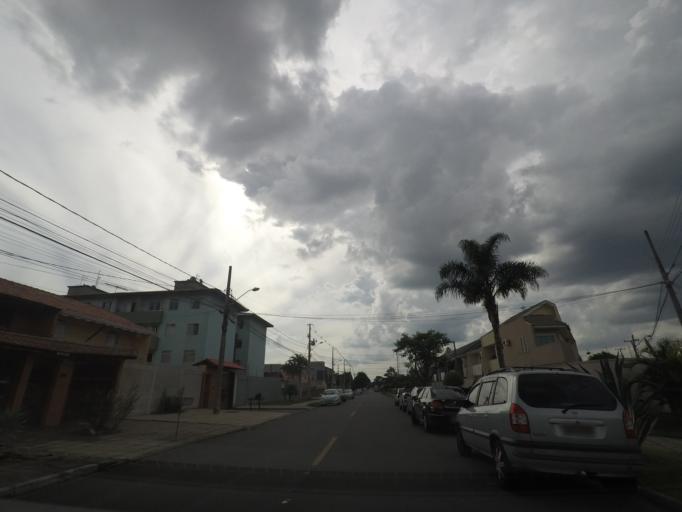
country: BR
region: Parana
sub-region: Sao Jose Dos Pinhais
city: Sao Jose dos Pinhais
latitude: -25.4890
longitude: -49.2462
